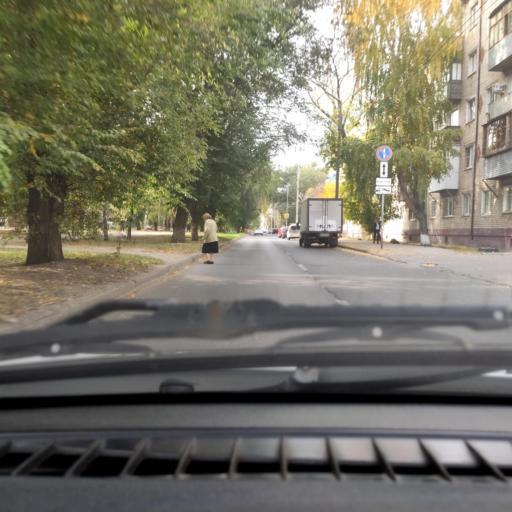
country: RU
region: Samara
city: Tol'yatti
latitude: 53.5160
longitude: 49.4221
